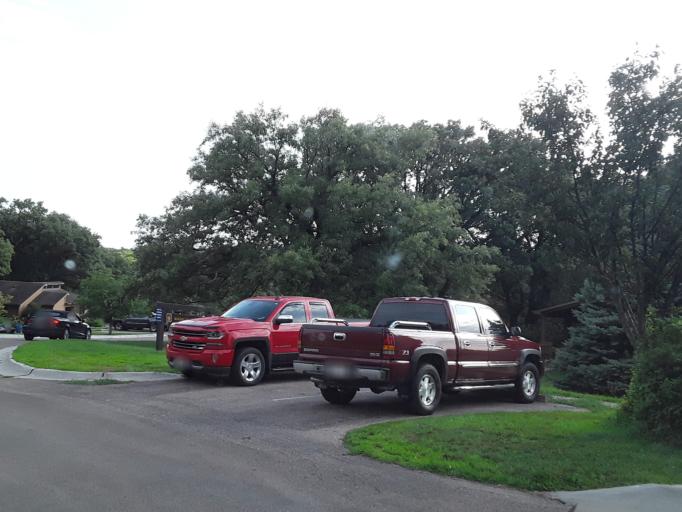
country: US
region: Nebraska
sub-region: Saunders County
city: Ashland
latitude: 41.0328
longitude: -96.3132
